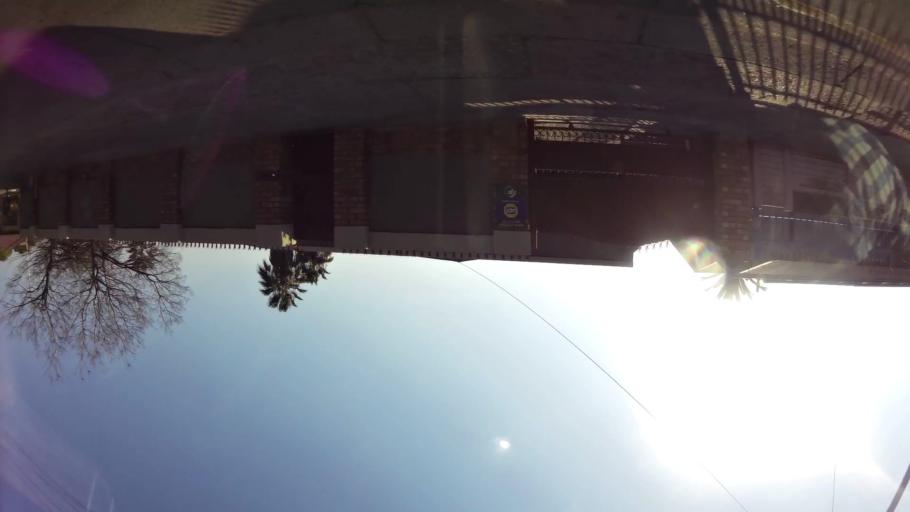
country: ZA
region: Gauteng
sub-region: City of Tshwane Metropolitan Municipality
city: Pretoria
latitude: -25.7571
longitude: 28.1237
